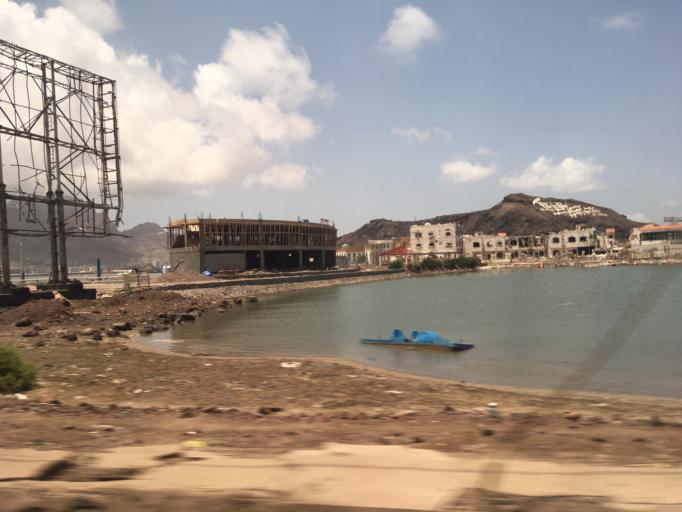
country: YE
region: Aden
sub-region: Khur Maksar
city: Khawr Maksar
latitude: 12.8112
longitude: 45.0238
